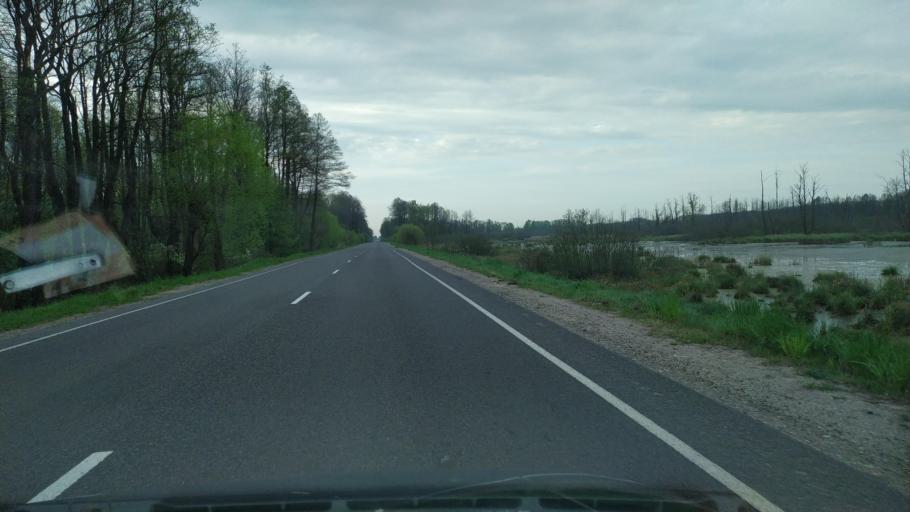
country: BY
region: Brest
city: Zhabinka
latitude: 52.2742
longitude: 23.9531
